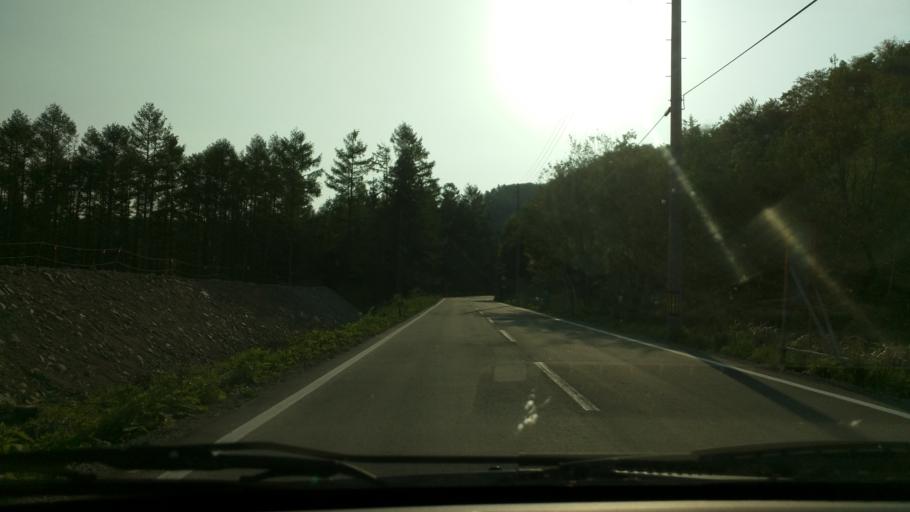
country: JP
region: Tochigi
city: Kuroiso
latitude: 37.2076
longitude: 139.9320
